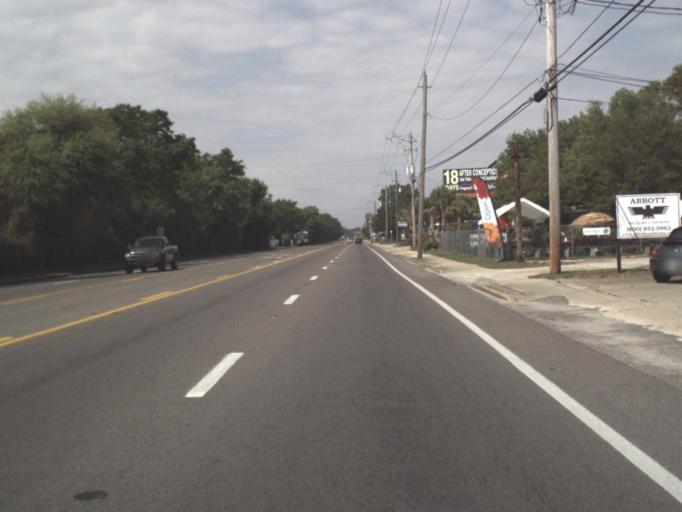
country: US
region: Florida
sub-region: Escambia County
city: Warrington
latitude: 30.3921
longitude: -87.2619
